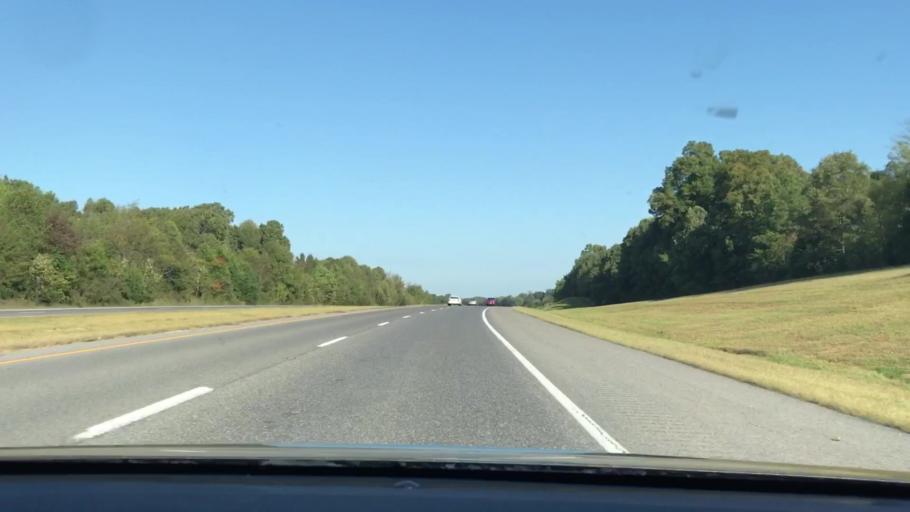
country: US
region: Kentucky
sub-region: Marshall County
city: Benton
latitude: 36.7786
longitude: -88.3217
